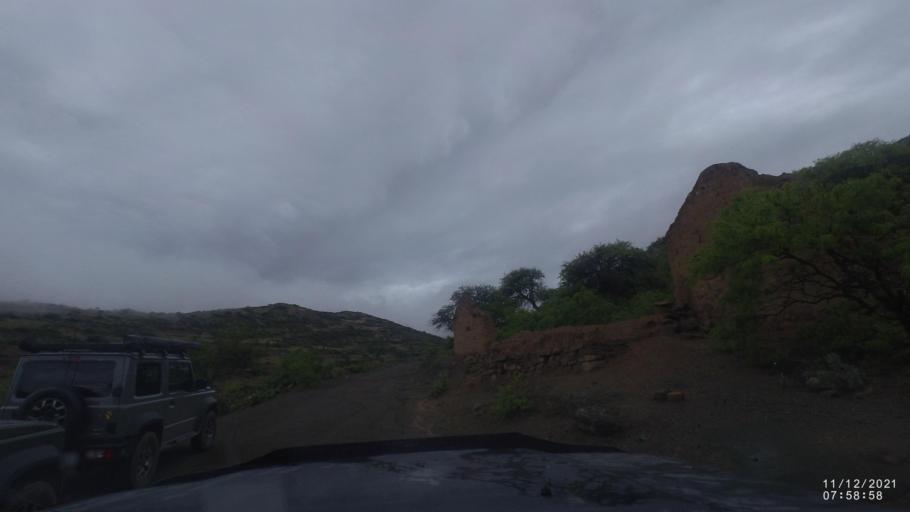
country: BO
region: Cochabamba
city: Tarata
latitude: -17.9454
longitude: -65.9271
